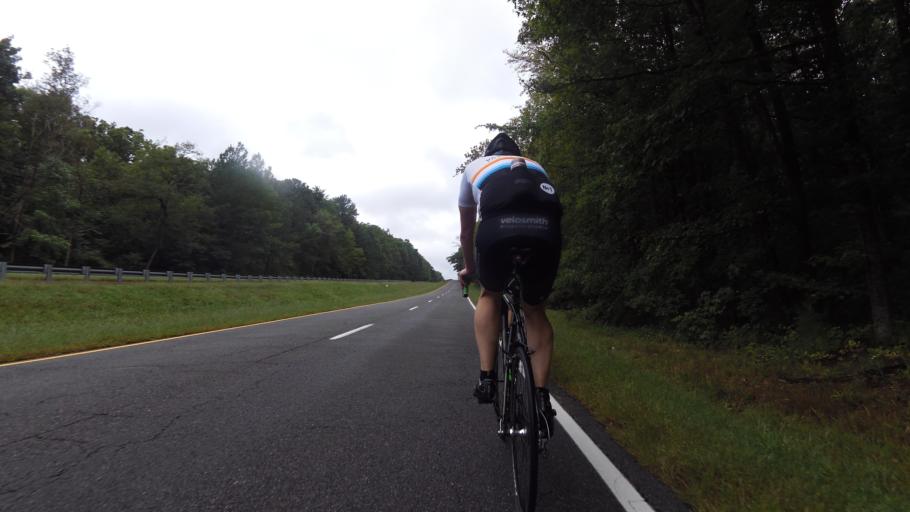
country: US
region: Virginia
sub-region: Henrico County
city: Short Pump
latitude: 37.6013
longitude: -77.6916
